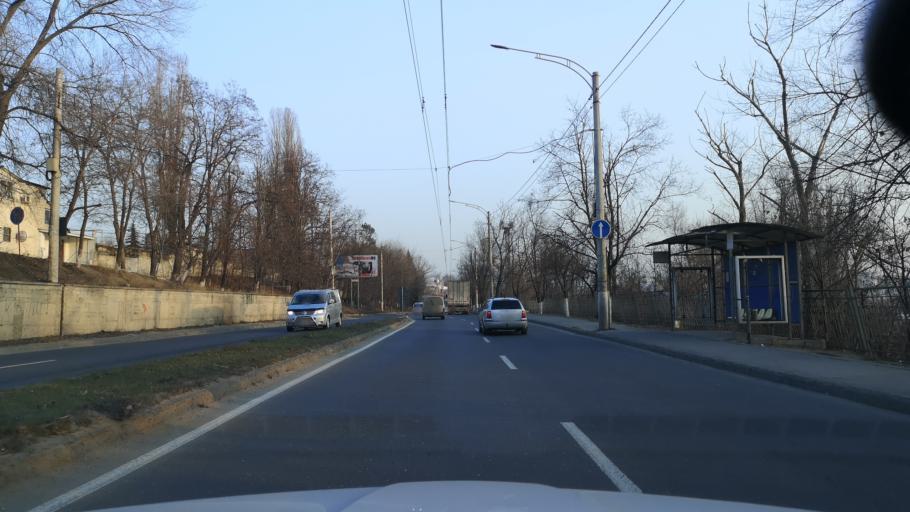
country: MD
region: Chisinau
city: Chisinau
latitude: 47.0497
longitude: 28.8228
